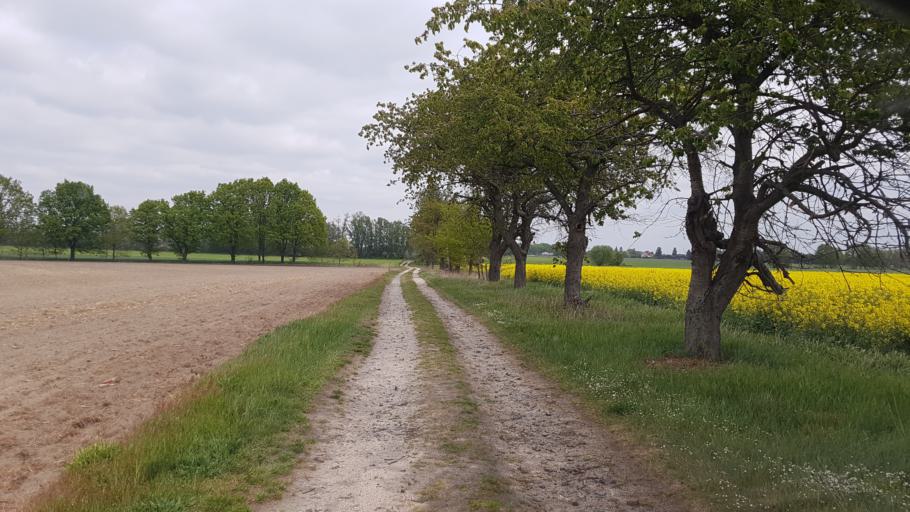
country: DE
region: Brandenburg
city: Sonnewalde
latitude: 51.6779
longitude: 13.6318
